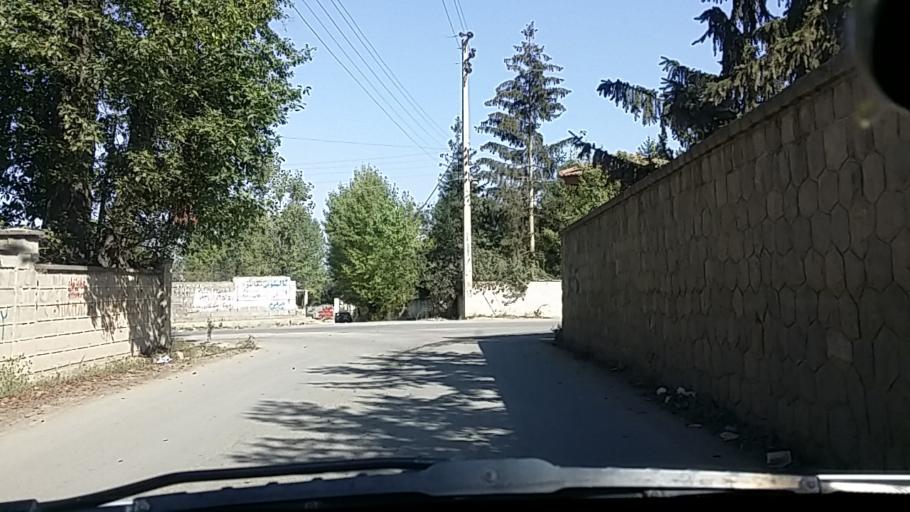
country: IR
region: Mazandaran
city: `Abbasabad
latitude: 36.5037
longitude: 51.1631
